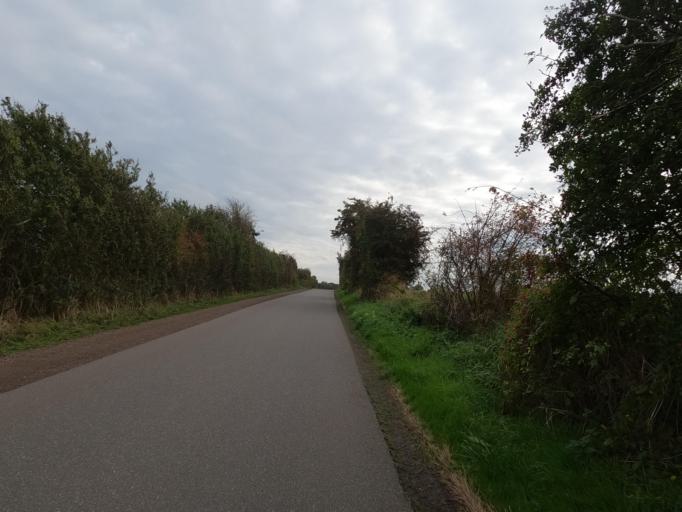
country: DE
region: Schleswig-Holstein
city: Neukirchen
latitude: 54.3561
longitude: 11.0316
